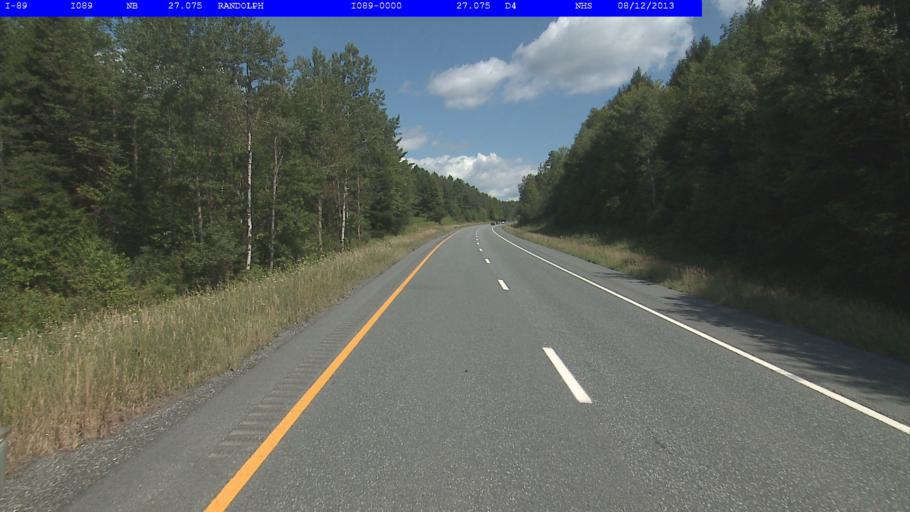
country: US
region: Vermont
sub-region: Orange County
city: Randolph
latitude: 43.8903
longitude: -72.6165
